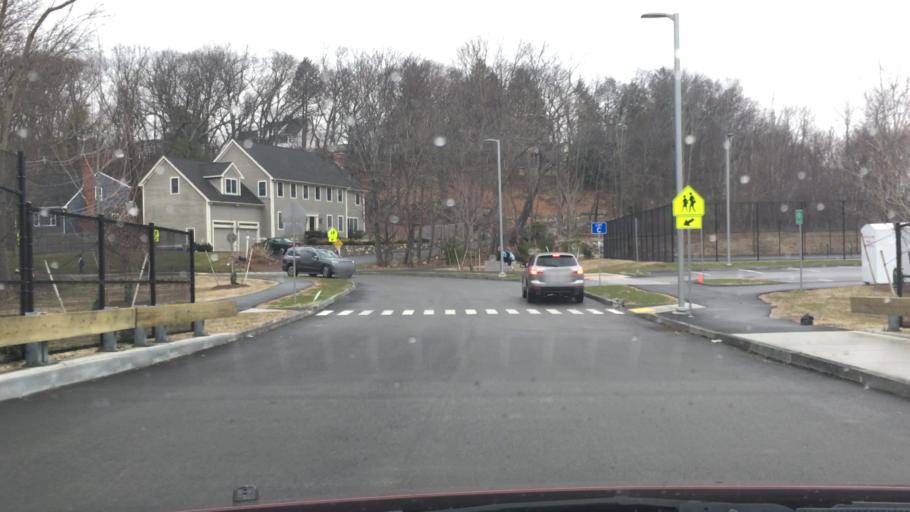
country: US
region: Massachusetts
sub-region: Middlesex County
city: Lexington
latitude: 42.4308
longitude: -71.2304
